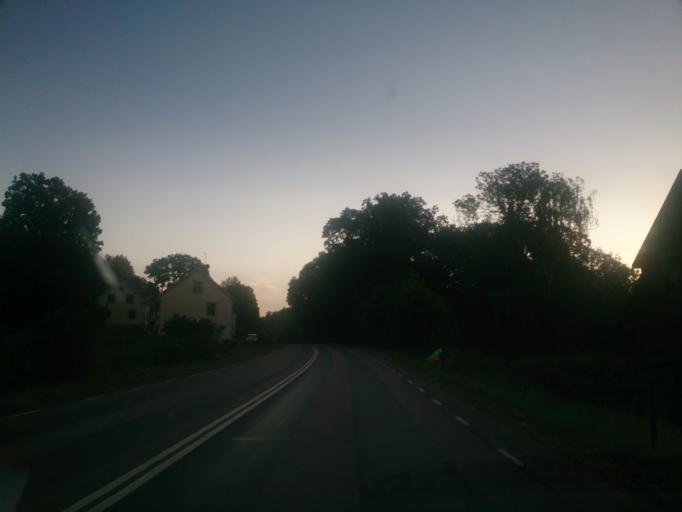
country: SE
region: Soedermanland
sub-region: Nykopings Kommun
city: Nykoping
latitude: 58.8191
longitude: 17.0912
